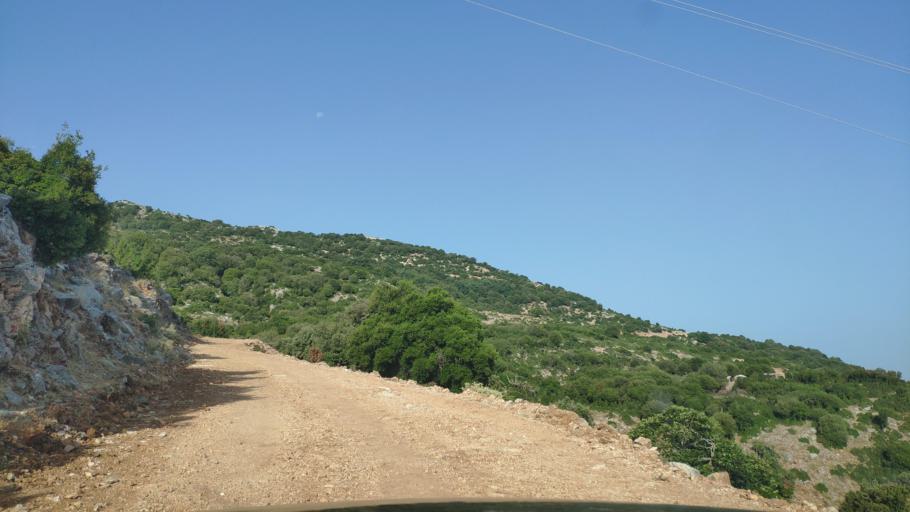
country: GR
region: West Greece
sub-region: Nomos Aitolias kai Akarnanias
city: Monastirakion
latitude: 38.8356
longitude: 20.9791
